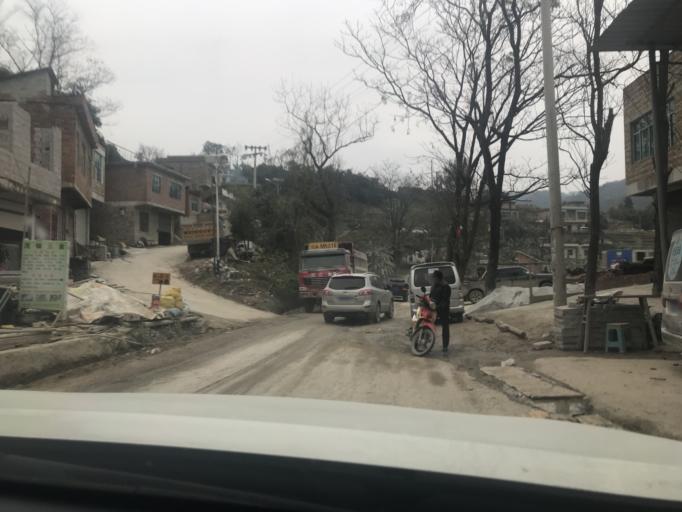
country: CN
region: Guangxi Zhuangzu Zizhiqu
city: Xinzhou
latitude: 24.9847
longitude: 105.8215
